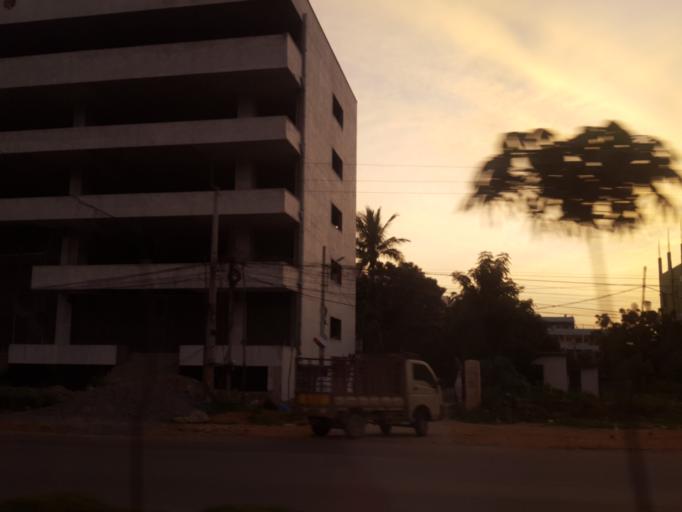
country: IN
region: Telangana
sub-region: Rangareddi
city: Kukatpalli
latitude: 17.5027
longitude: 78.3621
